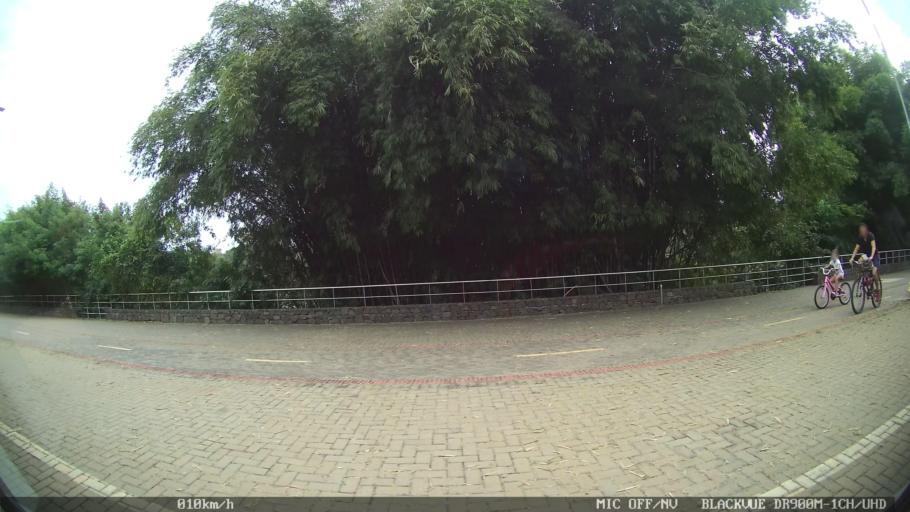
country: BR
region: Sao Paulo
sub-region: Piracicaba
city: Piracicaba
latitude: -22.7108
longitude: -47.6504
